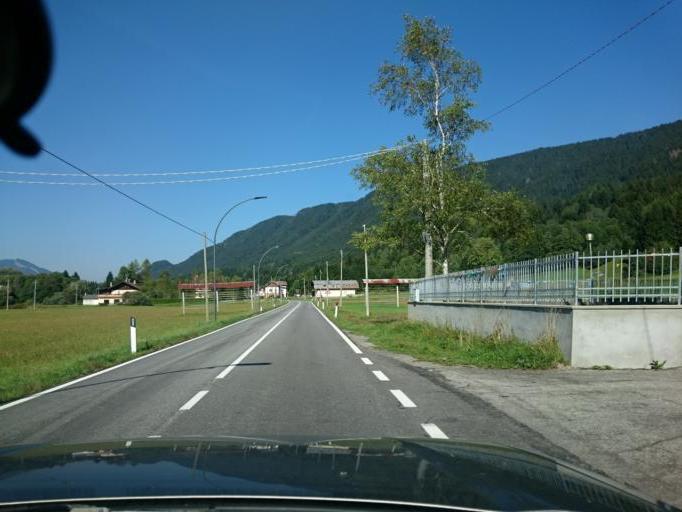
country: AT
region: Carinthia
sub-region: Politischer Bezirk Villach Land
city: Arnoldstein
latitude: 46.4979
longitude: 13.6950
